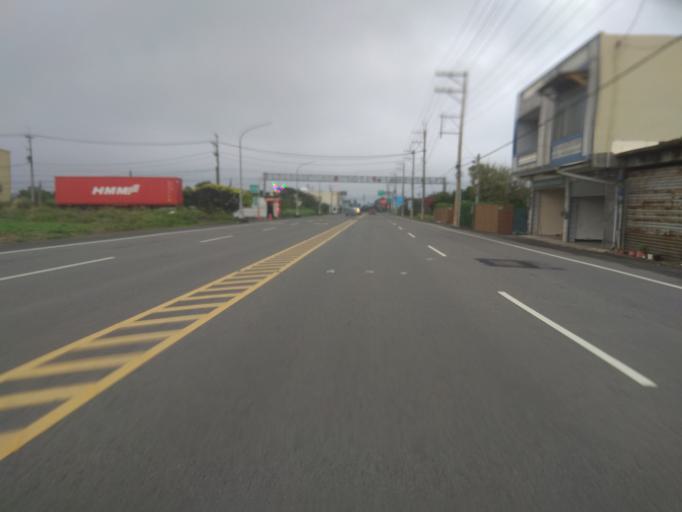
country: TW
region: Taiwan
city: Taoyuan City
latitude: 25.0327
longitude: 121.0973
